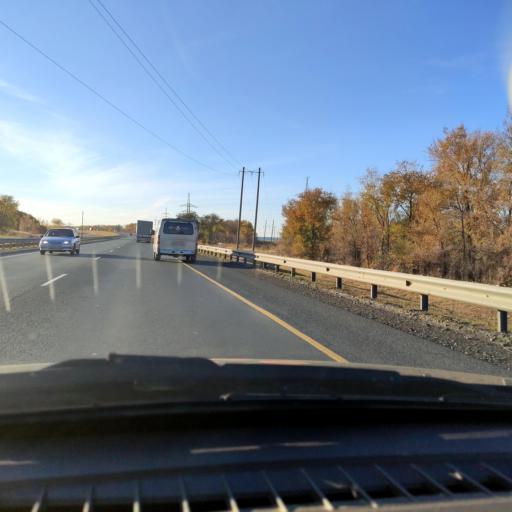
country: RU
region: Samara
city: Varlamovo
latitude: 53.1957
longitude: 48.3190
